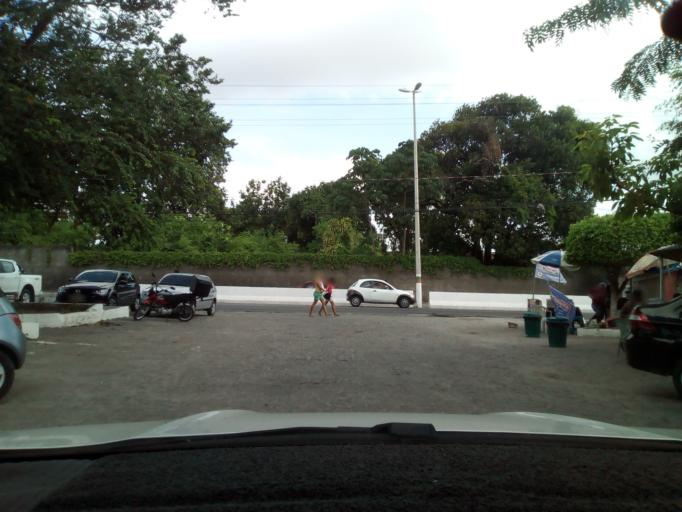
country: BR
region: Paraiba
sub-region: Bayeux
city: Bayeux
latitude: -7.1252
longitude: -34.9269
